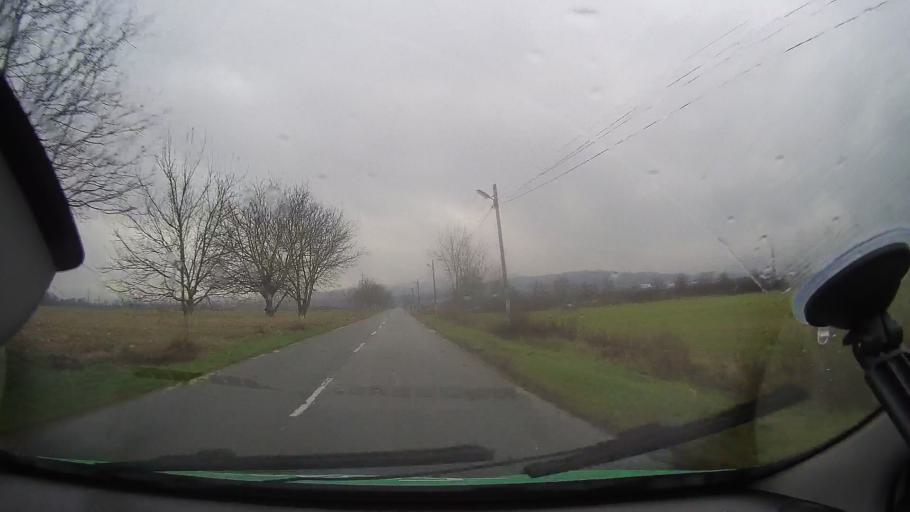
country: RO
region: Hunedoara
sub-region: Comuna Ribita
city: Ribita
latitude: 46.1691
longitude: 22.7656
